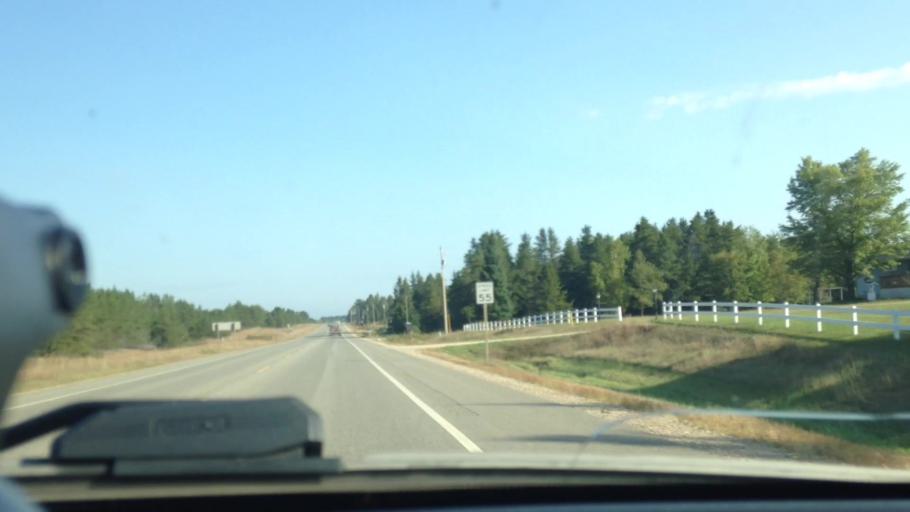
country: US
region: Wisconsin
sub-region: Marinette County
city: Niagara
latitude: 45.5697
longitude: -87.9969
